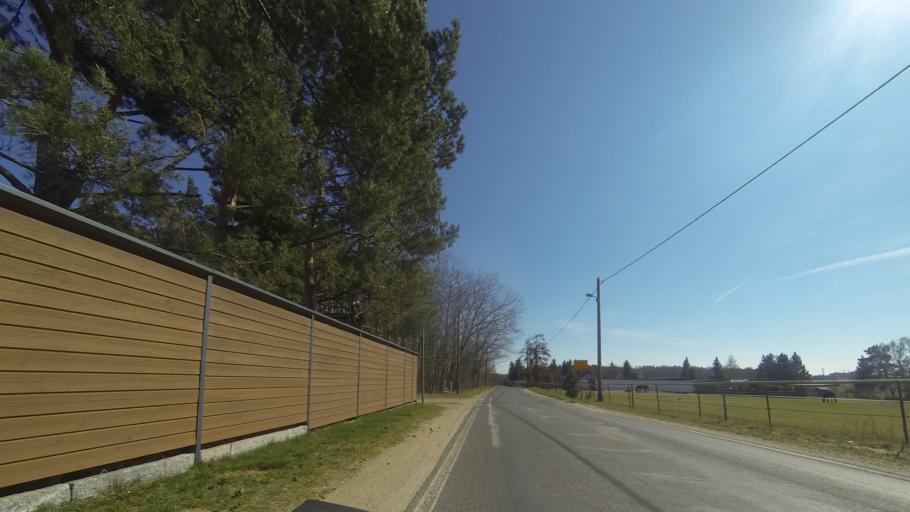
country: DE
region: Saxony
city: Ottendorf-Okrilla
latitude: 51.1673
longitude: 13.7926
